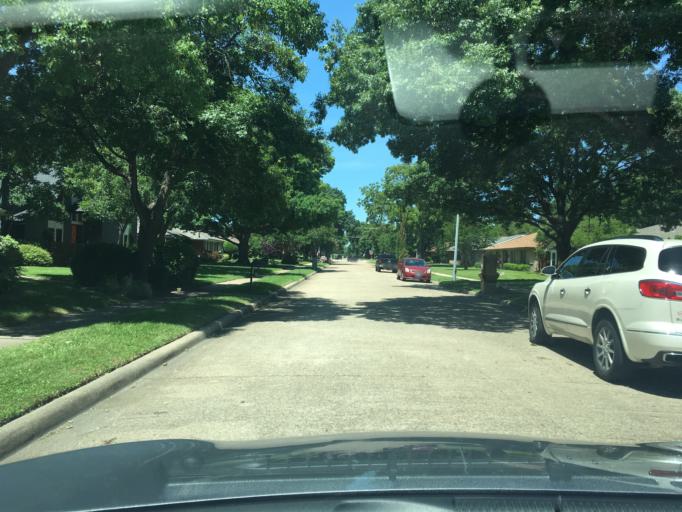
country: US
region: Texas
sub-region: Dallas County
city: Richardson
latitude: 32.9476
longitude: -96.6896
